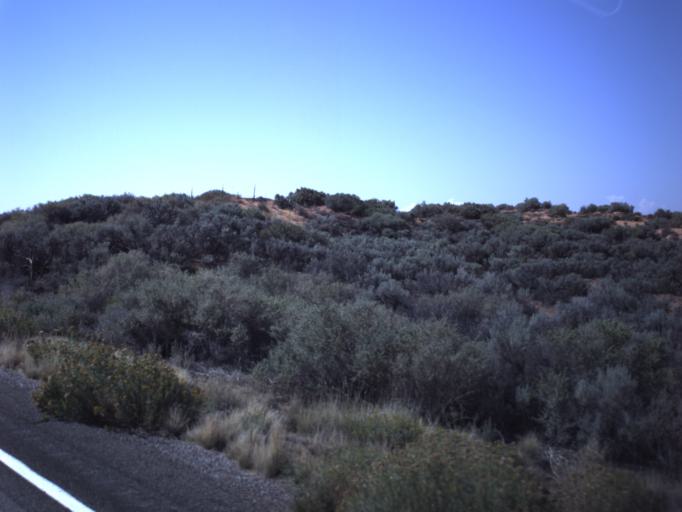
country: US
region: Utah
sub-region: San Juan County
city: Blanding
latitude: 37.0918
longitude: -109.5479
